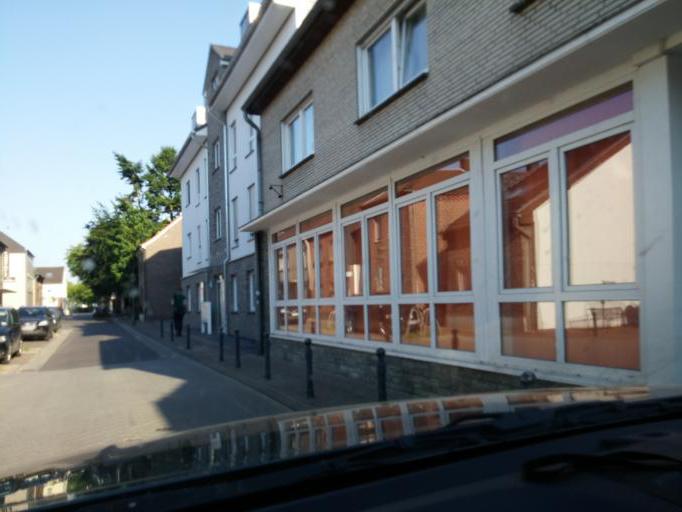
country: DE
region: North Rhine-Westphalia
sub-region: Regierungsbezirk Dusseldorf
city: Korschenbroich
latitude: 51.2515
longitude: 6.4747
